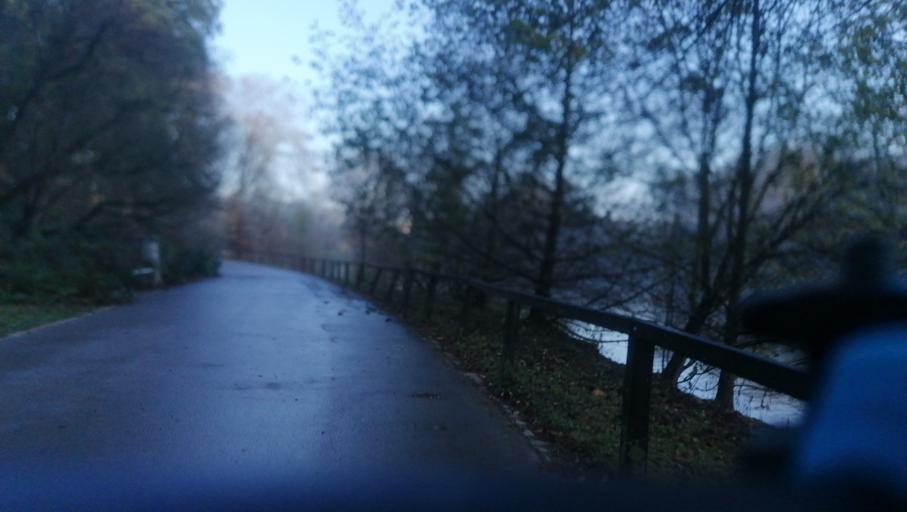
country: DE
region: North Rhine-Westphalia
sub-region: Regierungsbezirk Arnsberg
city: Dortmund
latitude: 51.4811
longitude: 7.4685
